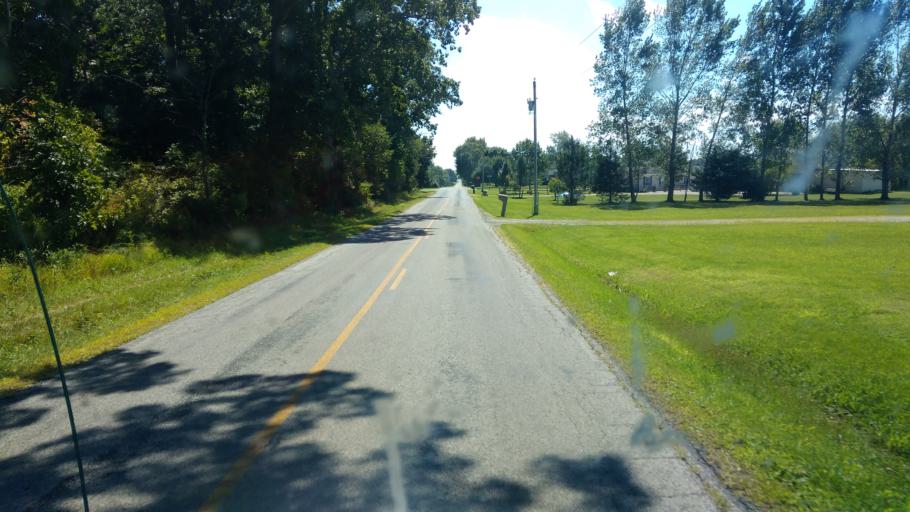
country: US
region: Ohio
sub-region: Marion County
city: Marion
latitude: 40.6602
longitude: -83.1733
